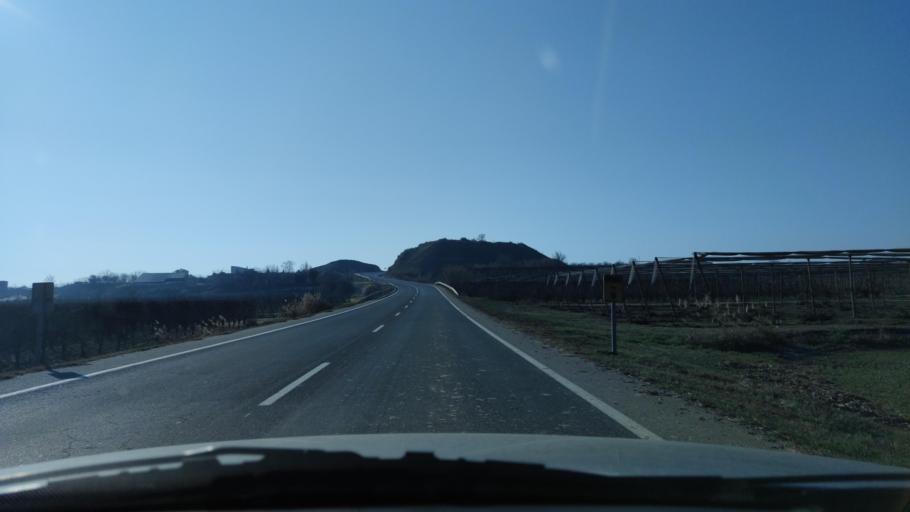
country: ES
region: Catalonia
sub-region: Provincia de Lleida
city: Torrefarrera
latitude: 41.7051
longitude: 0.6370
